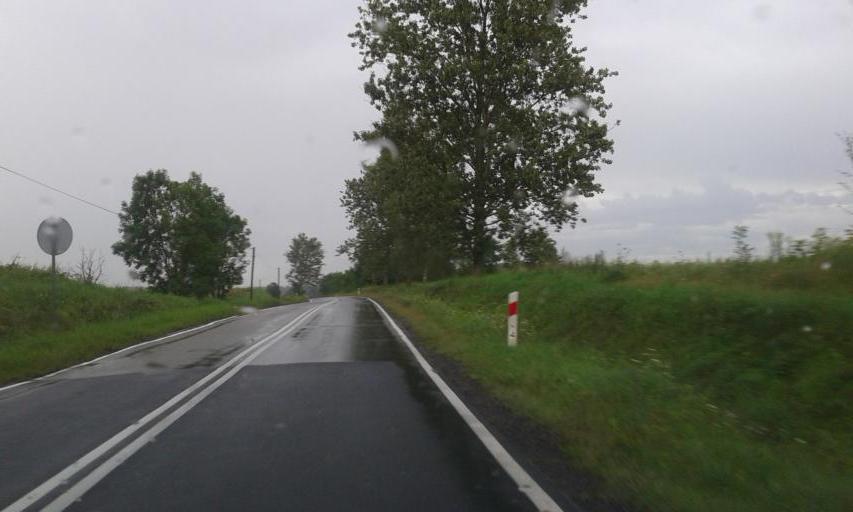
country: PL
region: West Pomeranian Voivodeship
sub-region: Powiat drawski
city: Czaplinek
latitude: 53.5636
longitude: 16.2504
